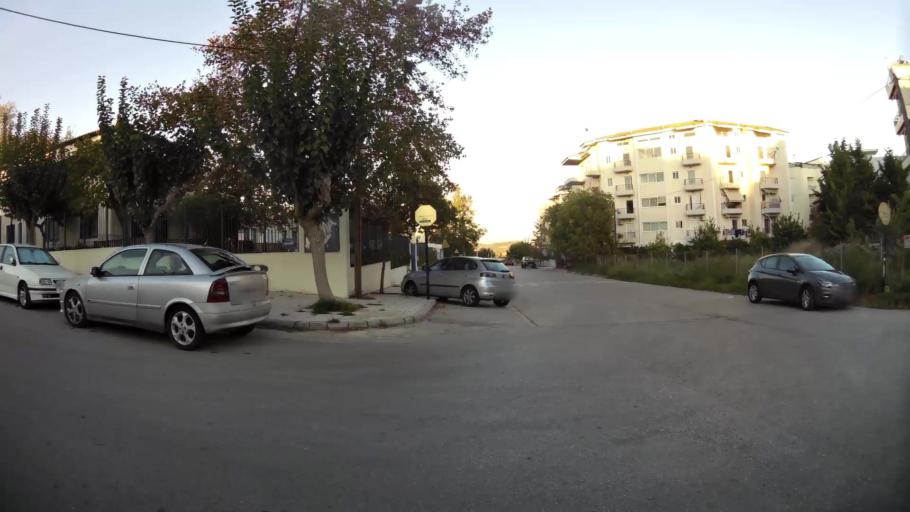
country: GR
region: Attica
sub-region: Nomarchia Anatolikis Attikis
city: Spata
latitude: 37.9647
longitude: 23.9225
